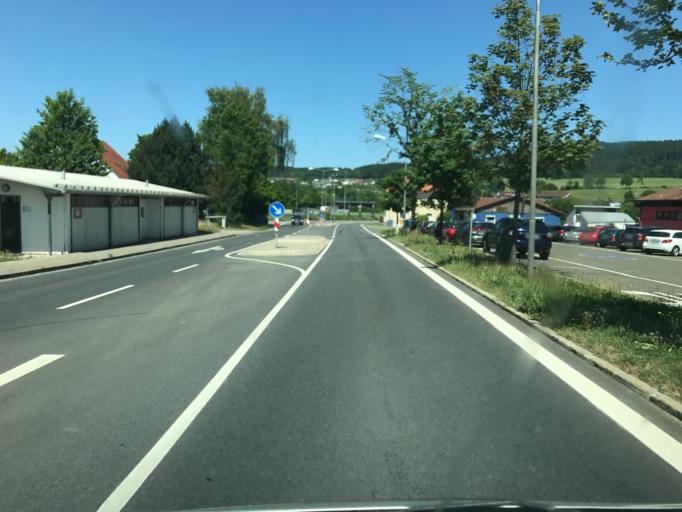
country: DE
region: Bavaria
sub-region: Upper Palatinate
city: Furth im Wald
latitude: 49.3383
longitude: 12.8471
